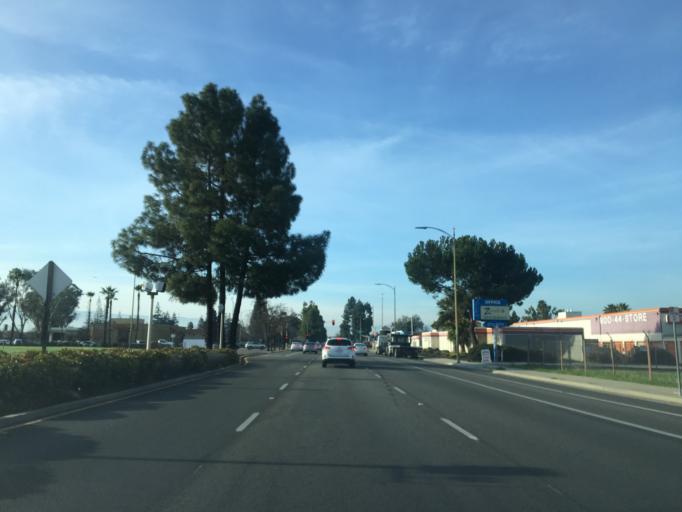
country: US
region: California
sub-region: Santa Clara County
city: Alum Rock
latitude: 37.3285
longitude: -121.8170
